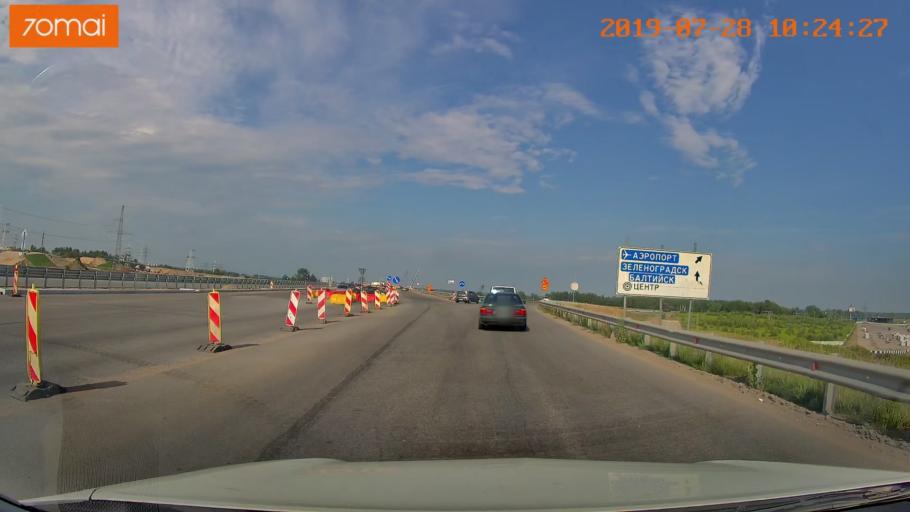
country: RU
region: Kaliningrad
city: Maloye Isakovo
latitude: 54.7682
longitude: 20.5516
